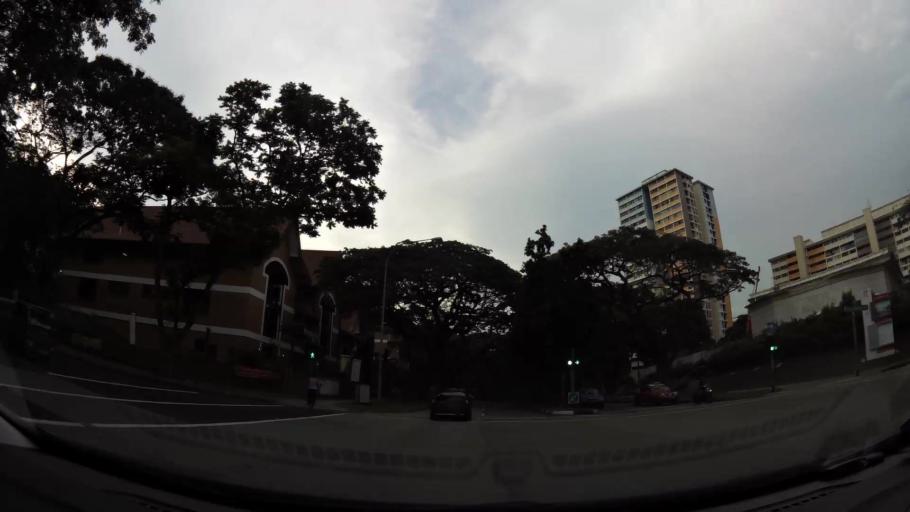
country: SG
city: Singapore
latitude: 1.2752
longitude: 103.8199
